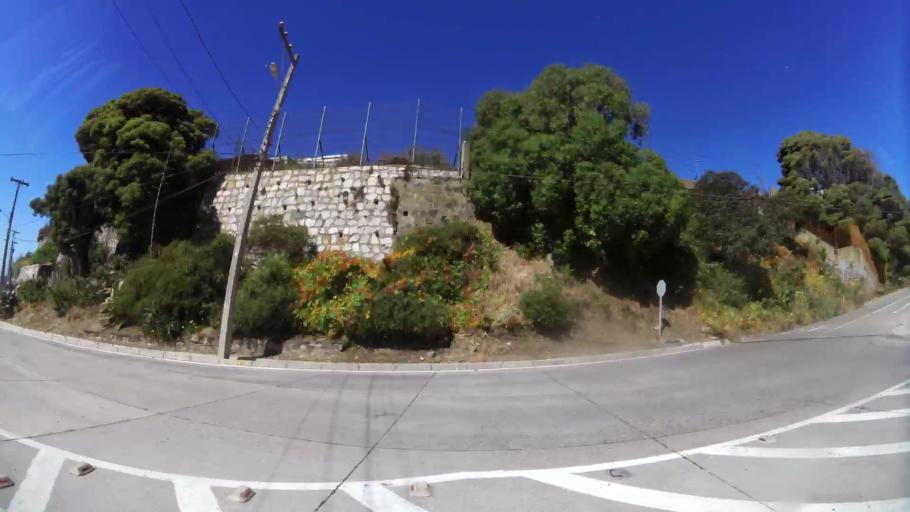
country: CL
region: Valparaiso
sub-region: Provincia de Valparaiso
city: Valparaiso
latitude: -33.0225
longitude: -71.6435
